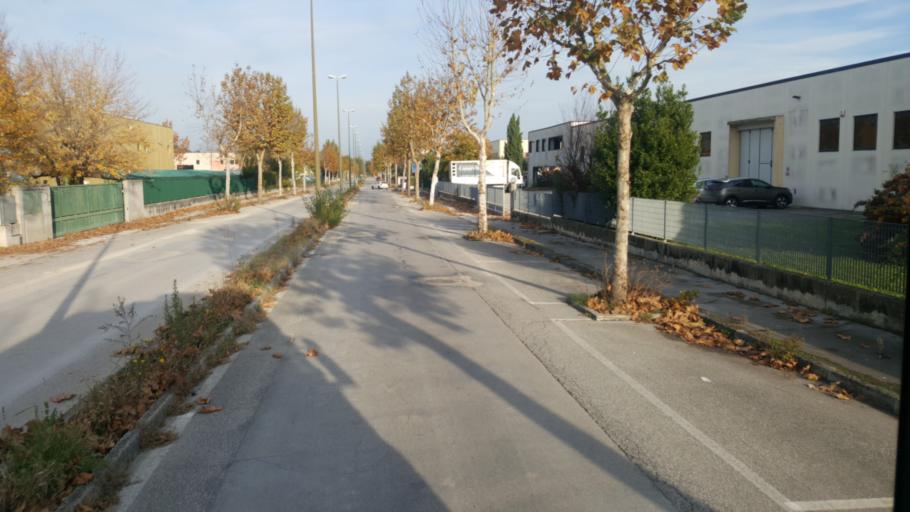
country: IT
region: The Marches
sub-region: Provincia di Ancona
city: Casine
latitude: 43.6456
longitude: 13.1396
